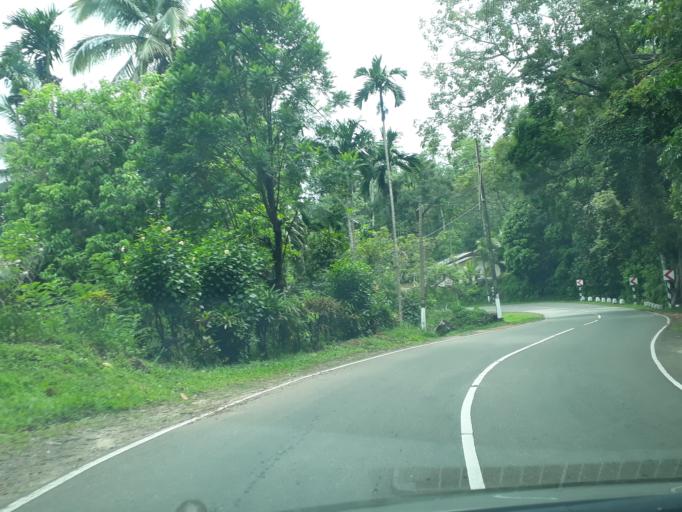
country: LK
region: Southern
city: Weligama
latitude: 6.3152
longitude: 80.5436
